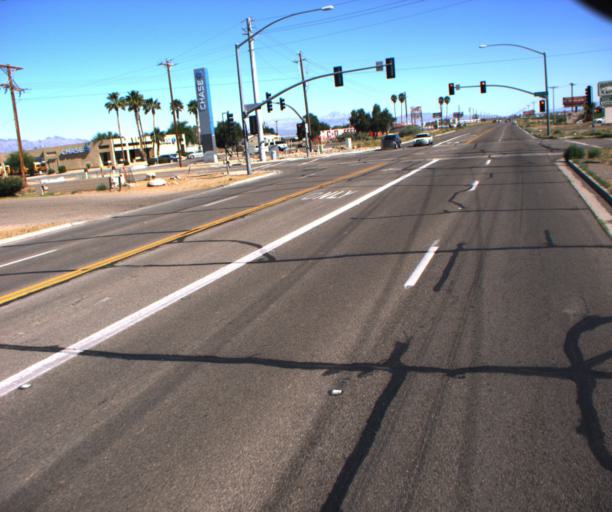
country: US
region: Arizona
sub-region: Mohave County
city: Willow Valley
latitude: 34.9092
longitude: -114.5977
